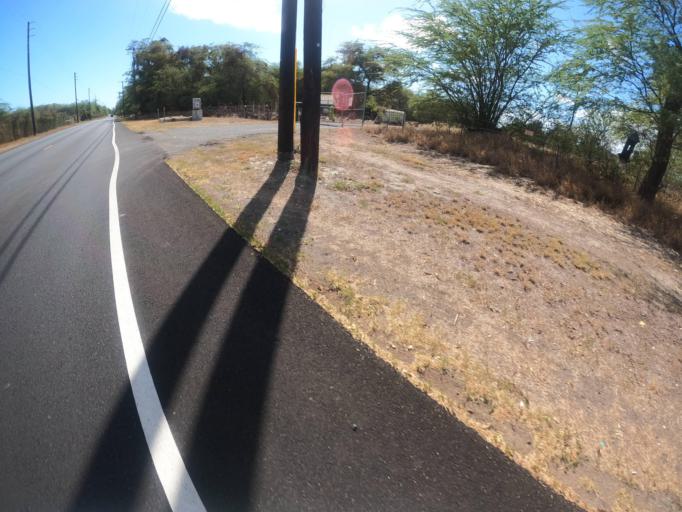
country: US
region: Hawaii
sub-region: Honolulu County
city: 'Ewa Villages
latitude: 21.3096
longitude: -158.0562
